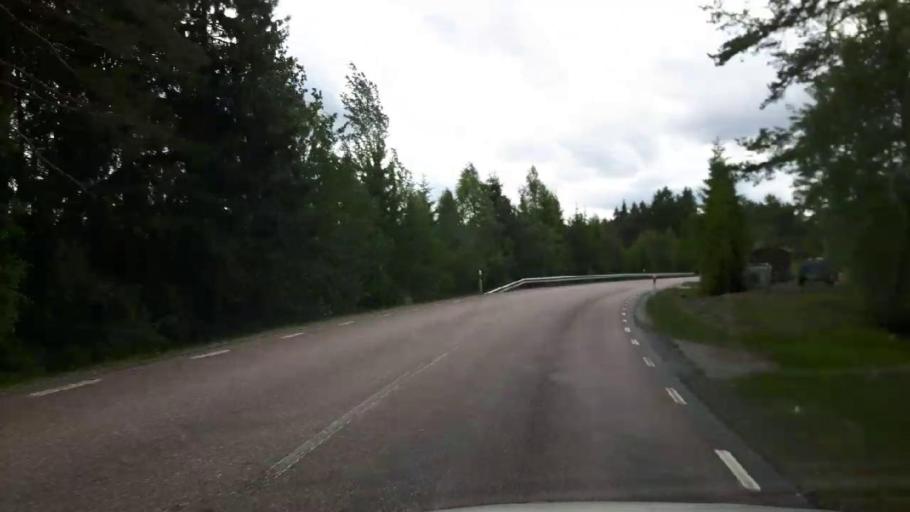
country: SE
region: Vaestmanland
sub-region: Fagersta Kommun
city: Fagersta
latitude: 59.8816
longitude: 15.8370
